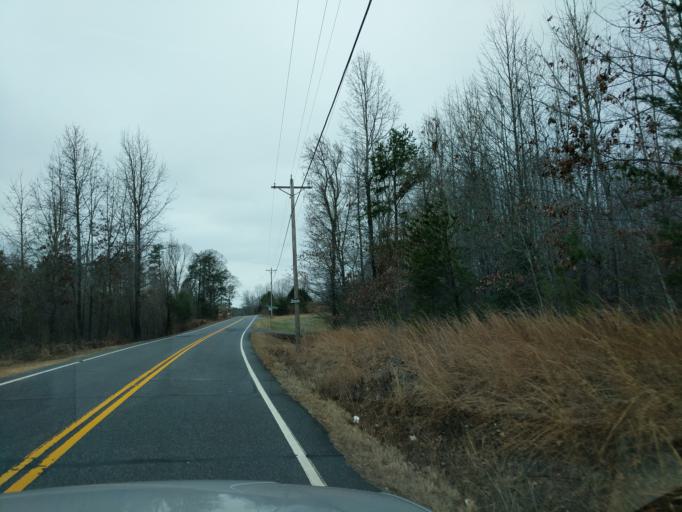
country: US
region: South Carolina
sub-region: Oconee County
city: Walhalla
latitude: 34.8250
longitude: -83.0447
